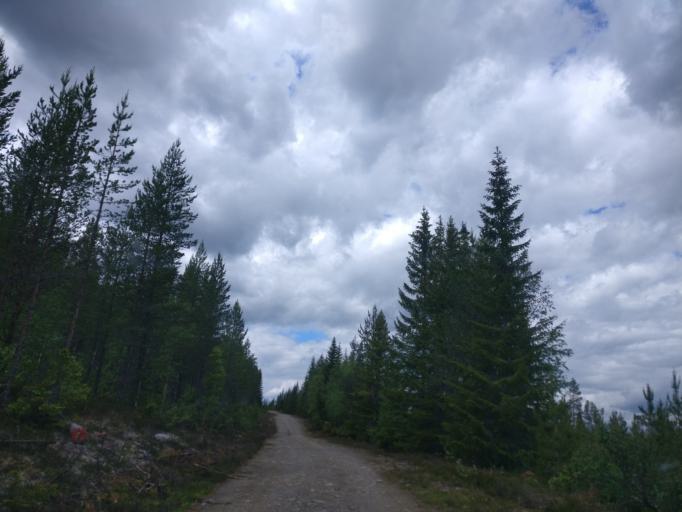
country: SE
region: Jaemtland
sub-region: Harjedalens Kommun
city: Sveg
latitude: 62.1969
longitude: 13.4119
